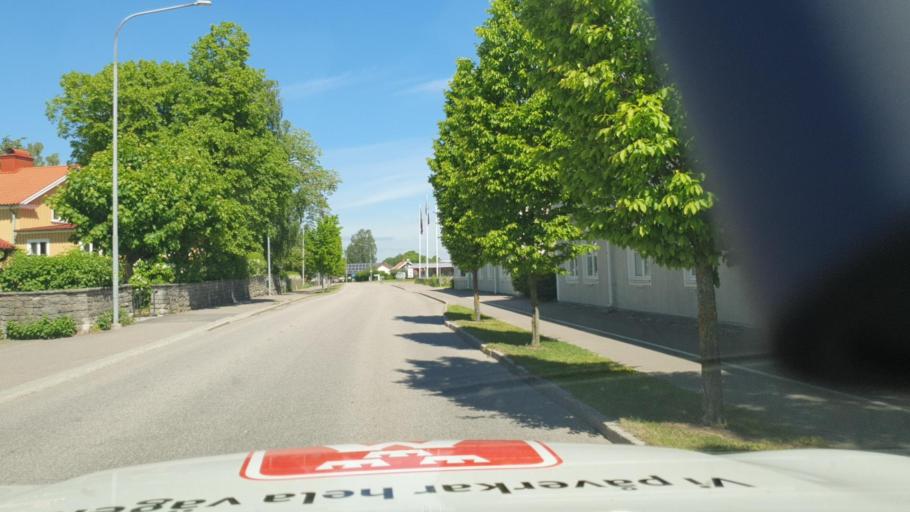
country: SE
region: Vaestra Goetaland
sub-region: Vara Kommun
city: Vara
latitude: 58.2669
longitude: 12.9540
